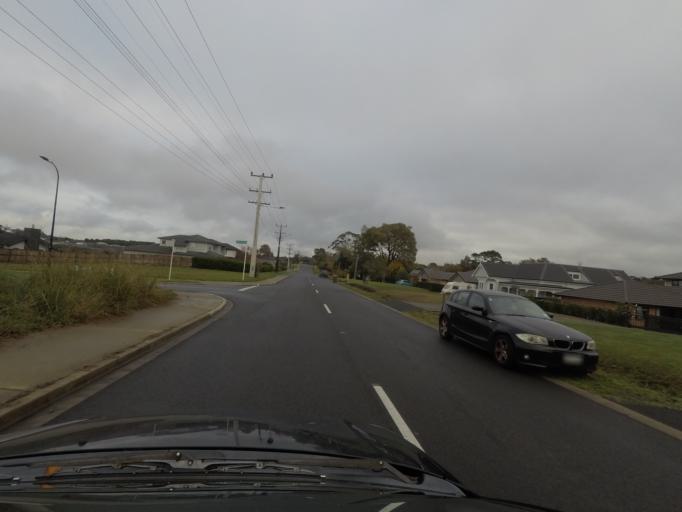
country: NZ
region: Auckland
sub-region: Auckland
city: Rosebank
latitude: -36.7630
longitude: 174.5948
